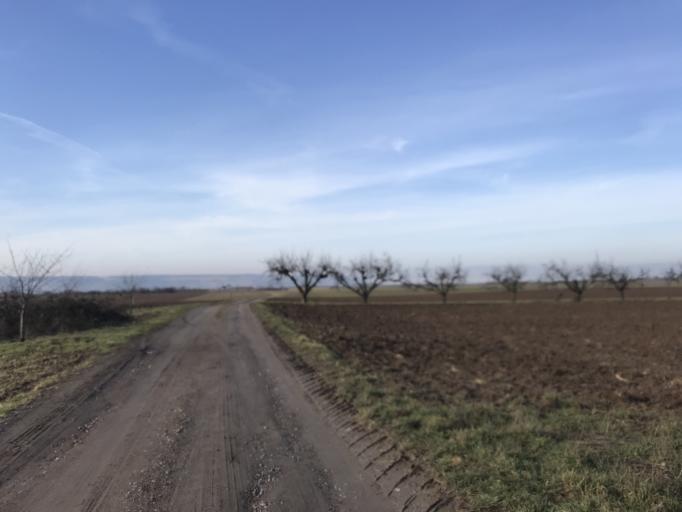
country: DE
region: Rheinland-Pfalz
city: Wackernheim
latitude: 49.9624
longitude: 8.0982
